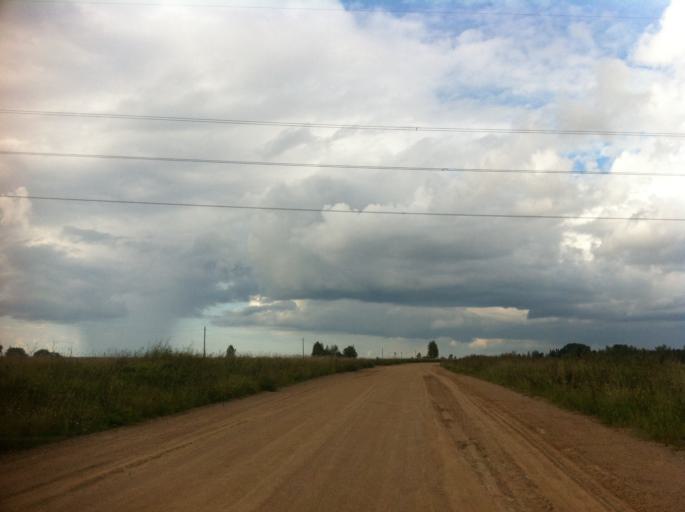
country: RU
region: Pskov
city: Izborsk
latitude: 57.8310
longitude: 27.9830
